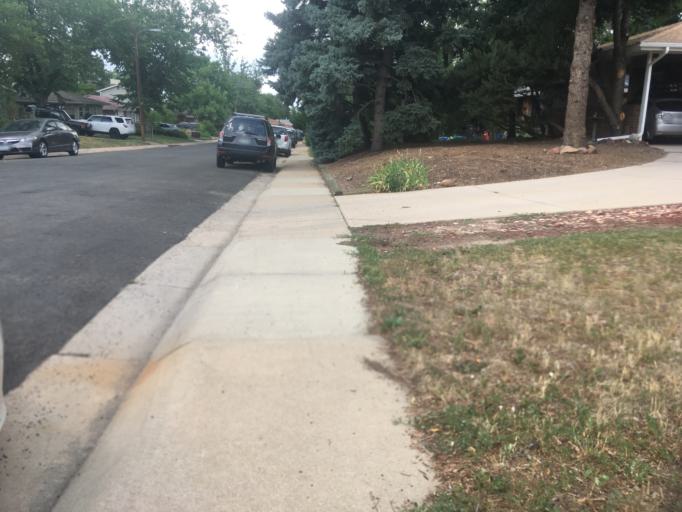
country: US
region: Colorado
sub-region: Boulder County
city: Boulder
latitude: 39.9862
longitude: -105.2464
